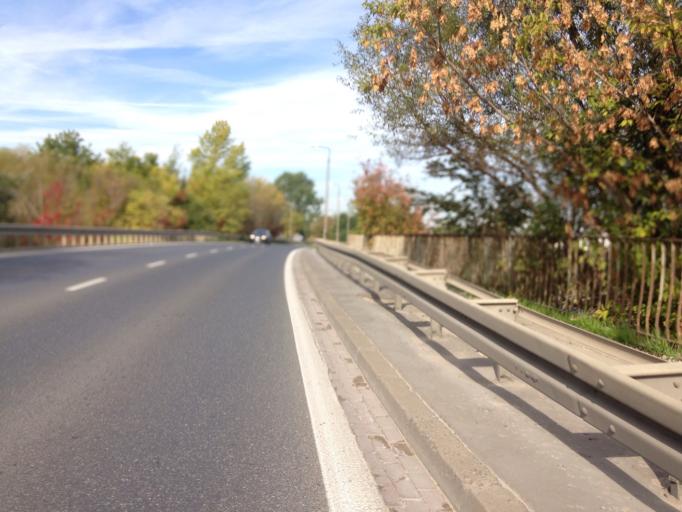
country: PL
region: Masovian Voivodeship
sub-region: Powiat wolominski
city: Zabki
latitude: 52.2624
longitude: 21.1240
